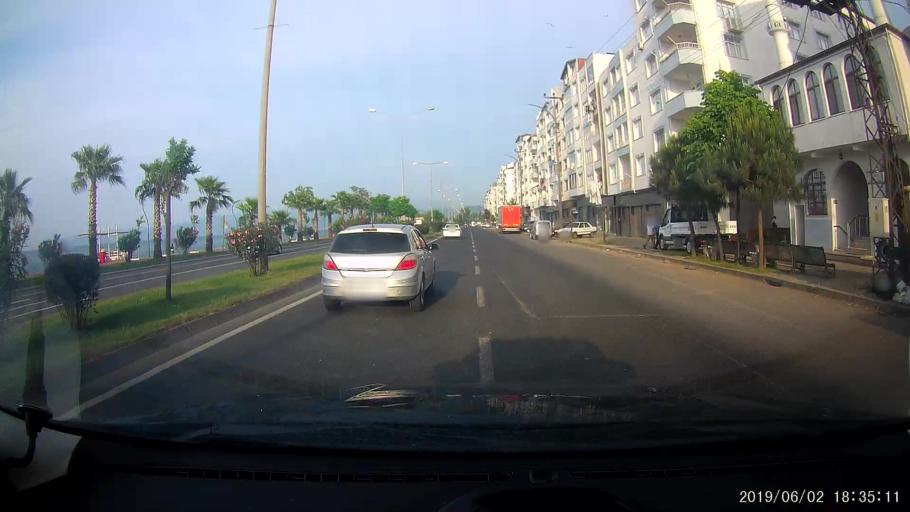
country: TR
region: Ordu
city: Fatsa
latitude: 41.0270
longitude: 37.5121
